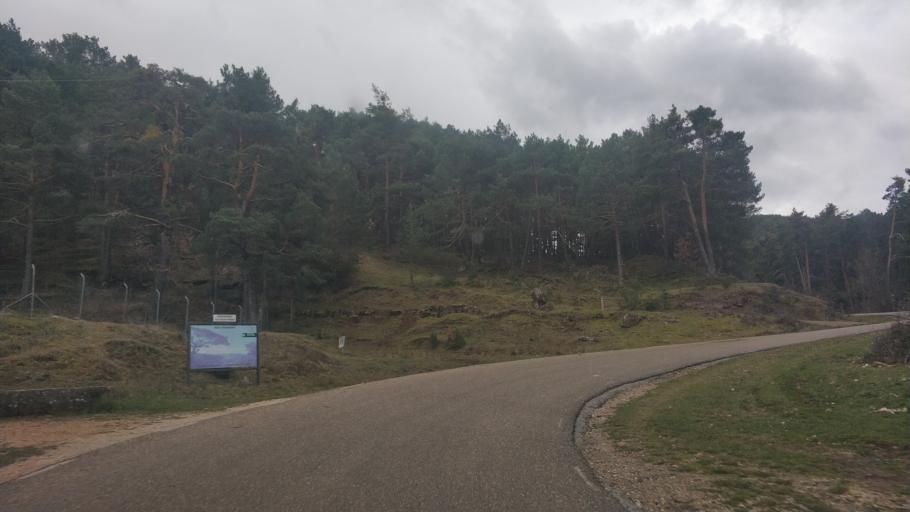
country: ES
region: Castille and Leon
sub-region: Provincia de Burgos
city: Canicosa de la Sierra
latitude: 41.9324
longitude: -3.0366
